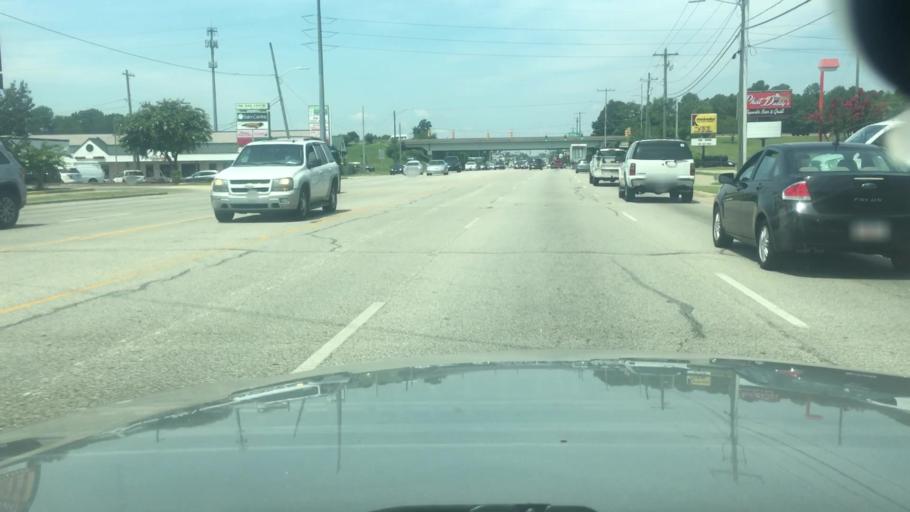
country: US
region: North Carolina
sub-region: Cumberland County
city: Fayetteville
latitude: 35.0443
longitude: -78.9368
